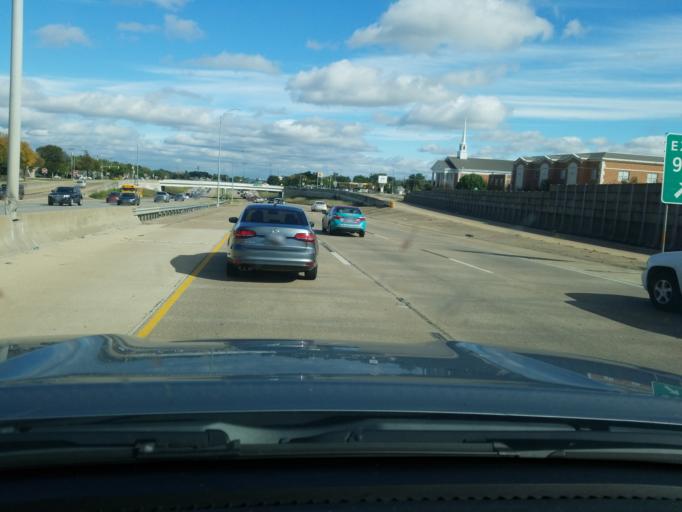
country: US
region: Texas
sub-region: Tarrant County
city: Westworth
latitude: 32.7346
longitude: -97.4168
